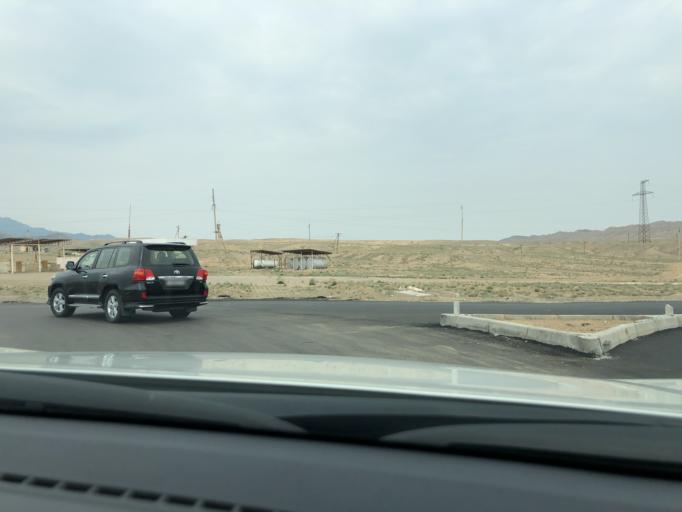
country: TJ
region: Viloyati Sughd
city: Kim
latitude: 40.1999
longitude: 70.4829
